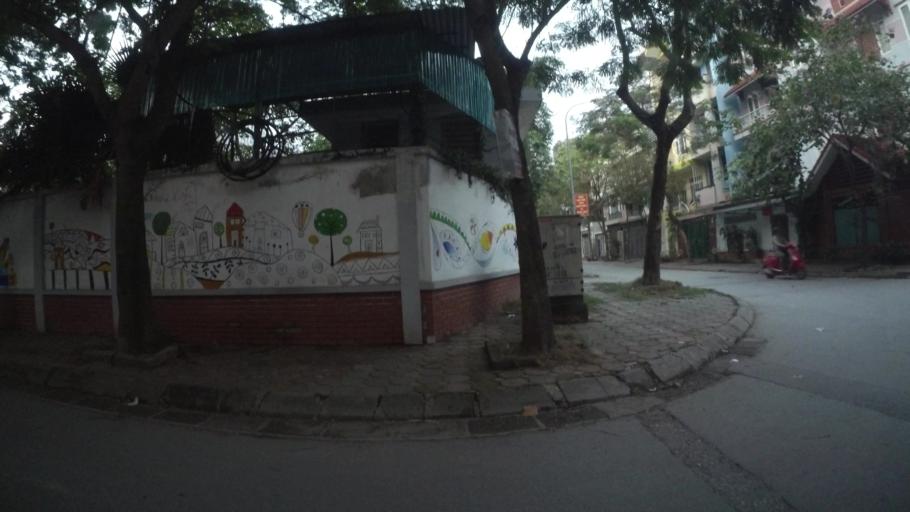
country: VN
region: Ha Noi
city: Ha Dong
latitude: 20.9726
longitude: 105.7870
